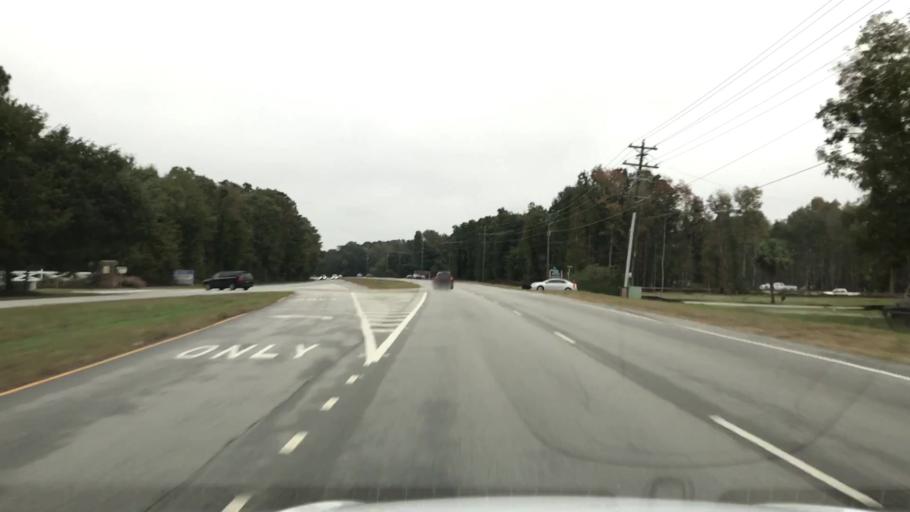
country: US
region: South Carolina
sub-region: Charleston County
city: Isle of Palms
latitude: 32.8871
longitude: -79.7446
